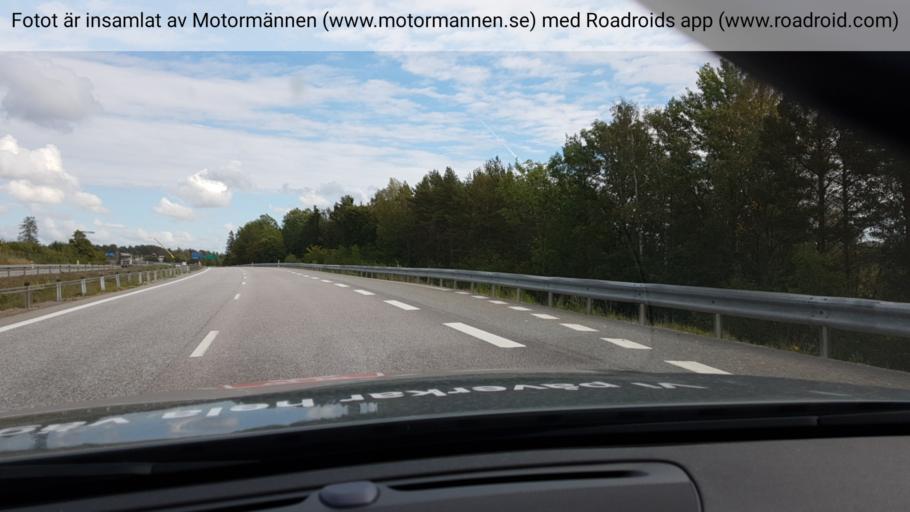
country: SE
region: Stockholm
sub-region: Norrtalje Kommun
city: Norrtalje
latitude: 59.7420
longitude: 18.6664
